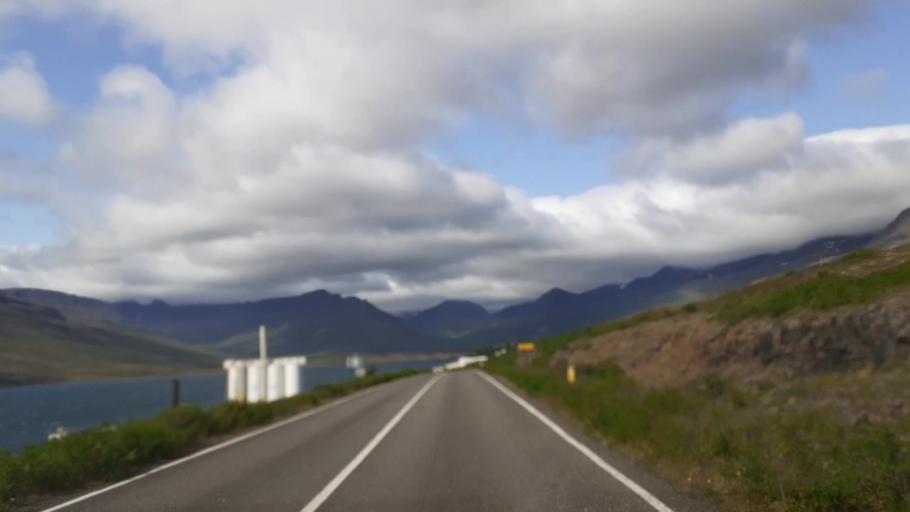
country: IS
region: East
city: Eskifjoerdur
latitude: 64.9242
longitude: -13.9838
